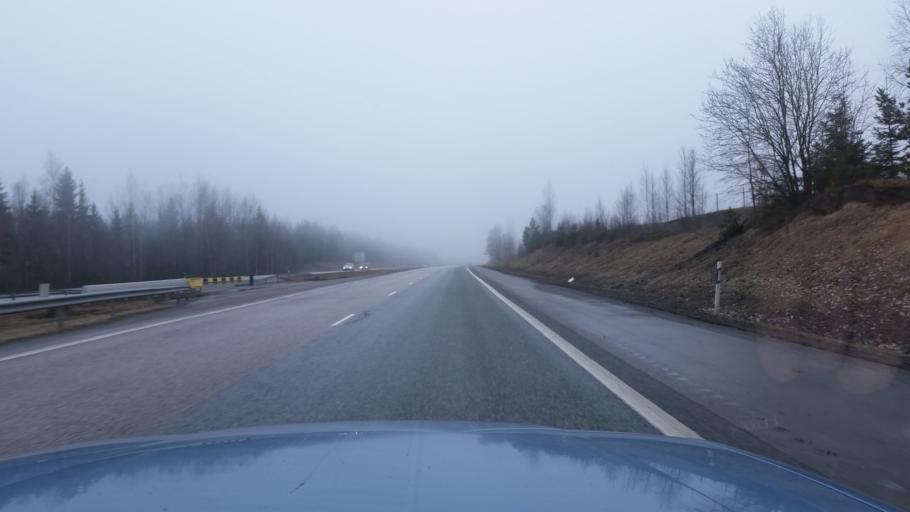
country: FI
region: Uusimaa
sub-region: Helsinki
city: Nurmijaervi
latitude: 60.4488
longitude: 24.8425
